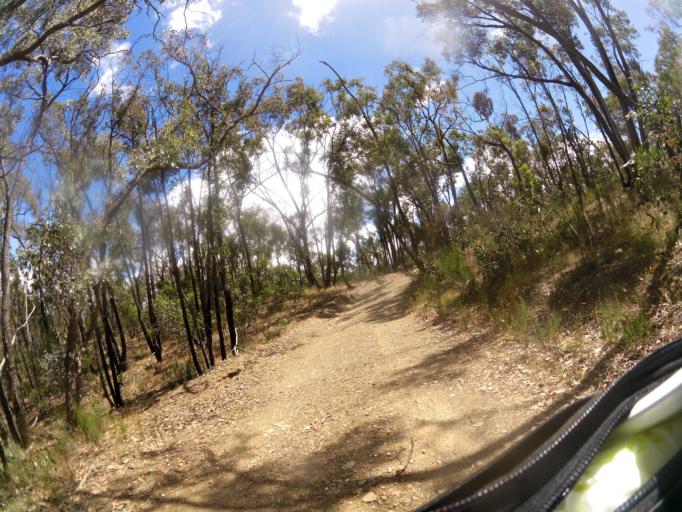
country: AU
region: Victoria
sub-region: Mount Alexander
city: Castlemaine
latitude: -37.0709
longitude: 144.2631
